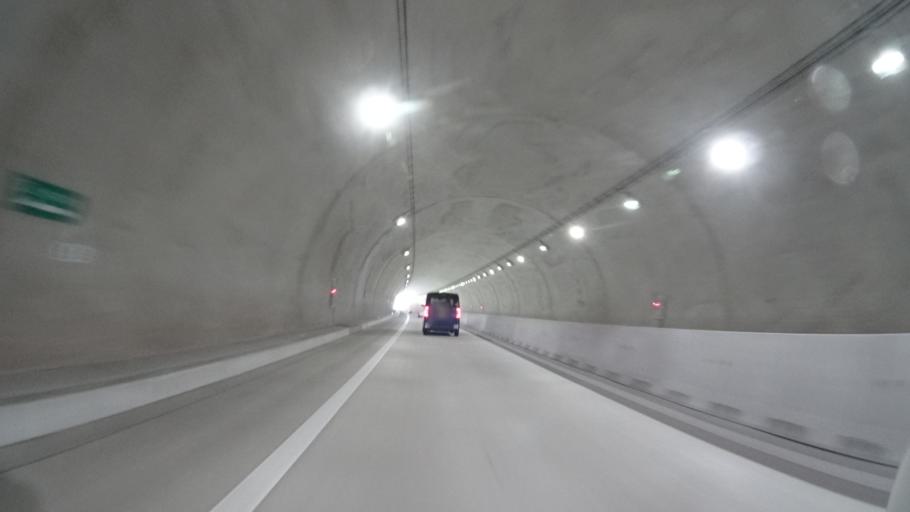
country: JP
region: Kumamoto
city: Ozu
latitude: 32.7456
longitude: 130.8420
